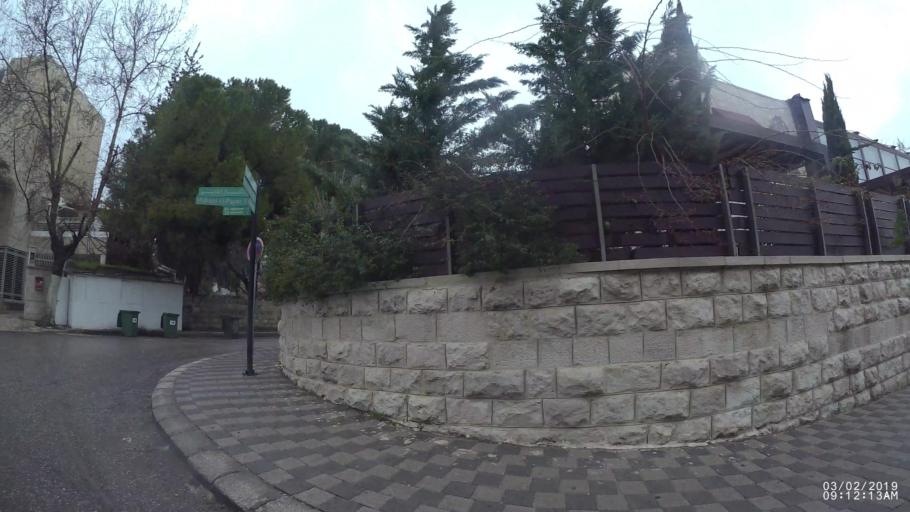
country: JO
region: Amman
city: Amman
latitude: 31.9525
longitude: 35.9072
